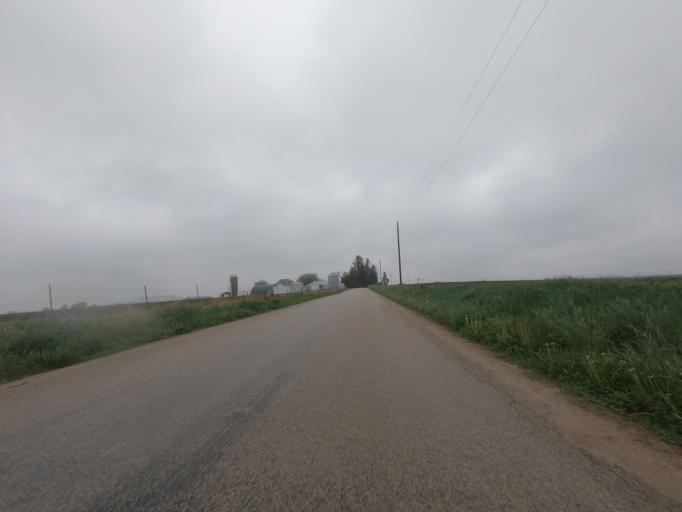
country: US
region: Wisconsin
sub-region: Grant County
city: Hazel Green
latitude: 42.5048
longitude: -90.5096
